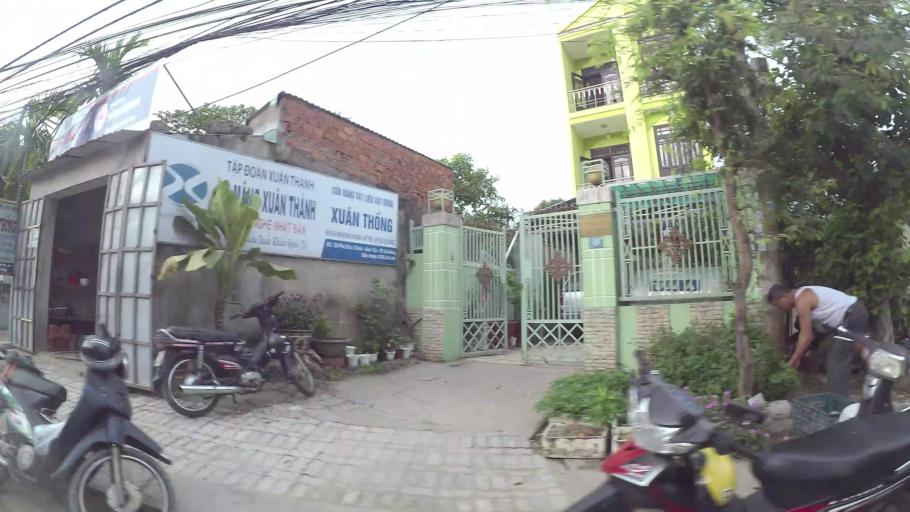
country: VN
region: Da Nang
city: Son Tra
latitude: 16.0828
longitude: 108.2397
